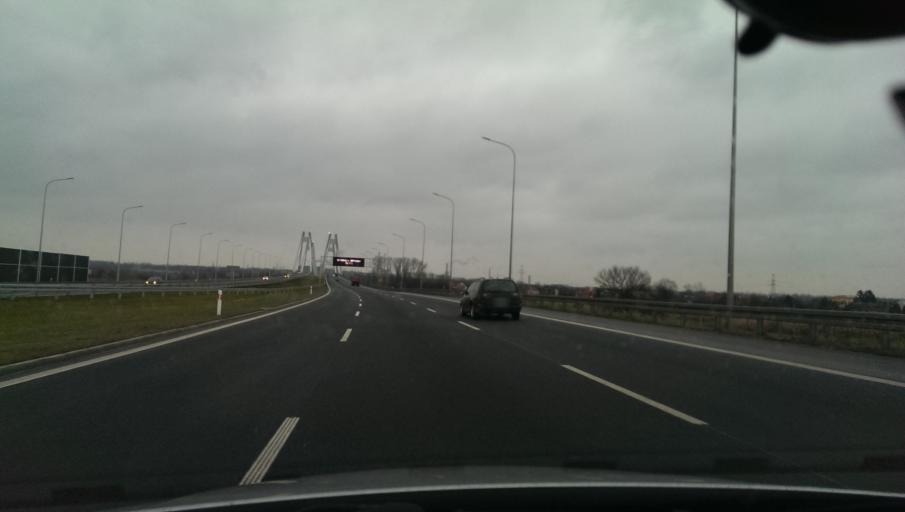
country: PL
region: Lesser Poland Voivodeship
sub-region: Powiat wielicki
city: Kokotow
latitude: 50.0438
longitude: 20.0693
